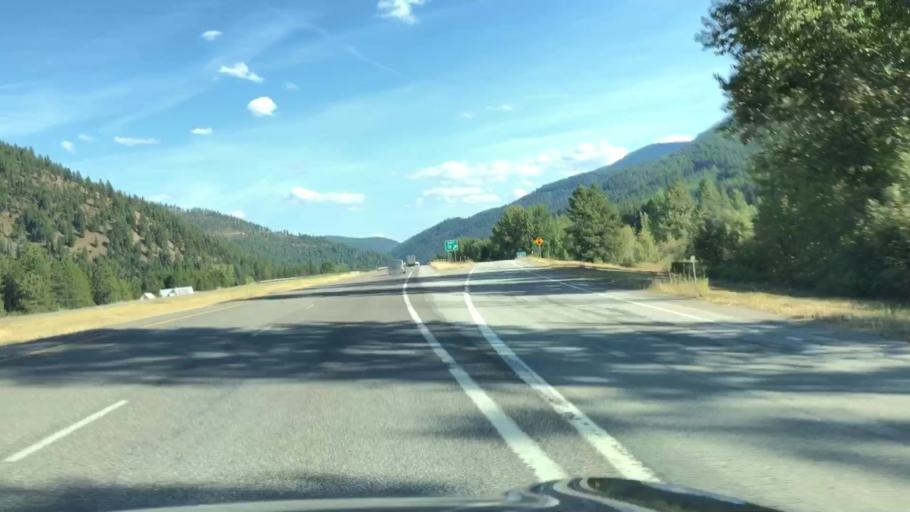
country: US
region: Montana
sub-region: Sanders County
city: Thompson Falls
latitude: 47.3776
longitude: -115.3541
